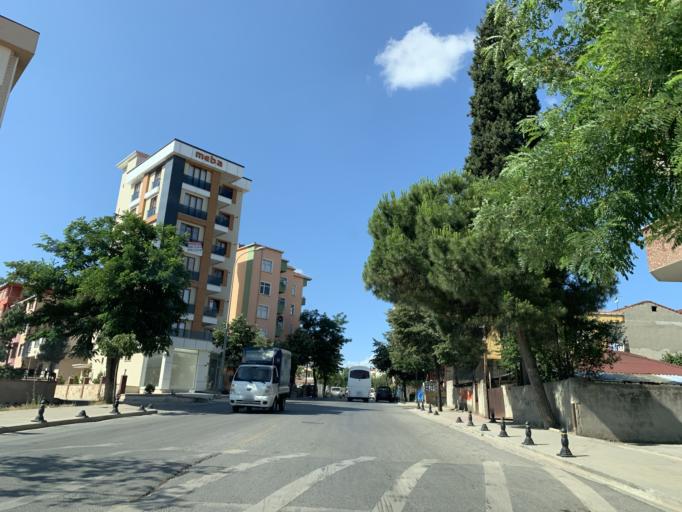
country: TR
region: Istanbul
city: Pendik
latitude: 40.8827
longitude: 29.2824
